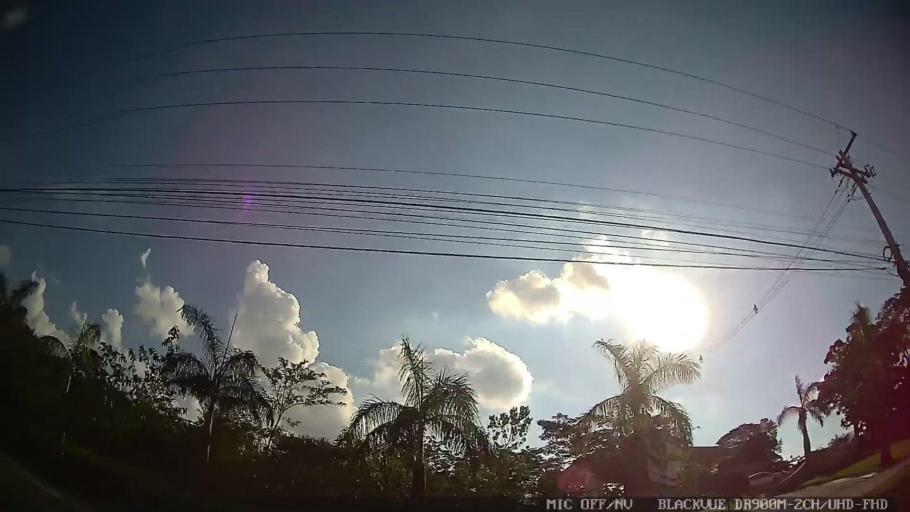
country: BR
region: Sao Paulo
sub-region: Braganca Paulista
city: Braganca Paulista
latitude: -22.9711
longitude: -46.5099
